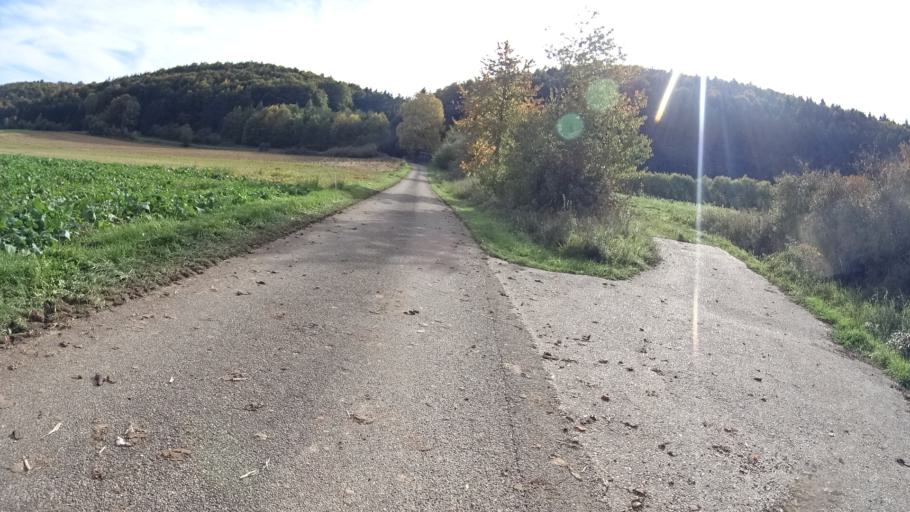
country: DE
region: Bavaria
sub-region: Upper Bavaria
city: Walting
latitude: 48.9296
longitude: 11.3271
